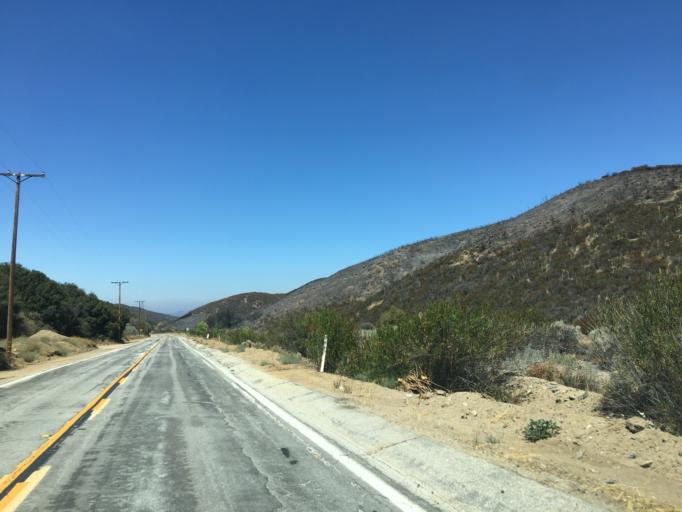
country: US
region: California
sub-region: Los Angeles County
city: Leona Valley
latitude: 34.5834
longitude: -118.3280
